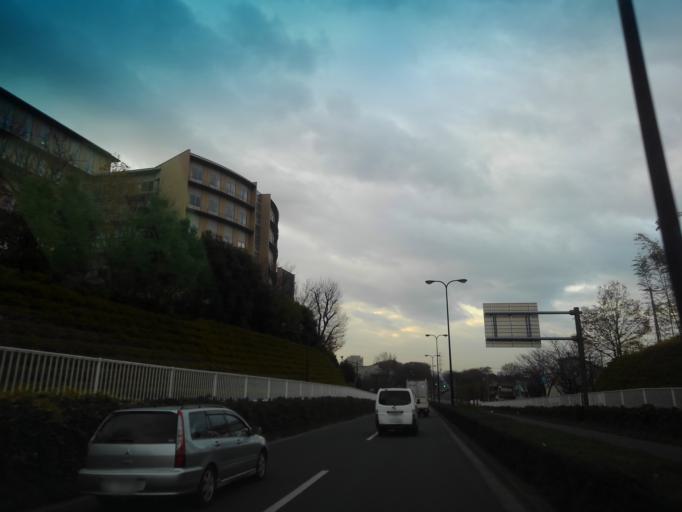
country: JP
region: Tokyo
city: Kokubunji
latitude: 35.6926
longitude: 139.4600
